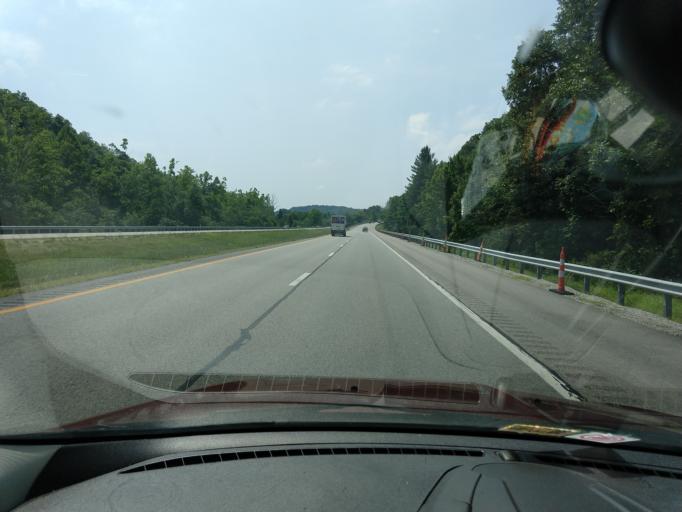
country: US
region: West Virginia
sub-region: Jackson County
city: Ripley
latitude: 38.6963
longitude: -81.6410
